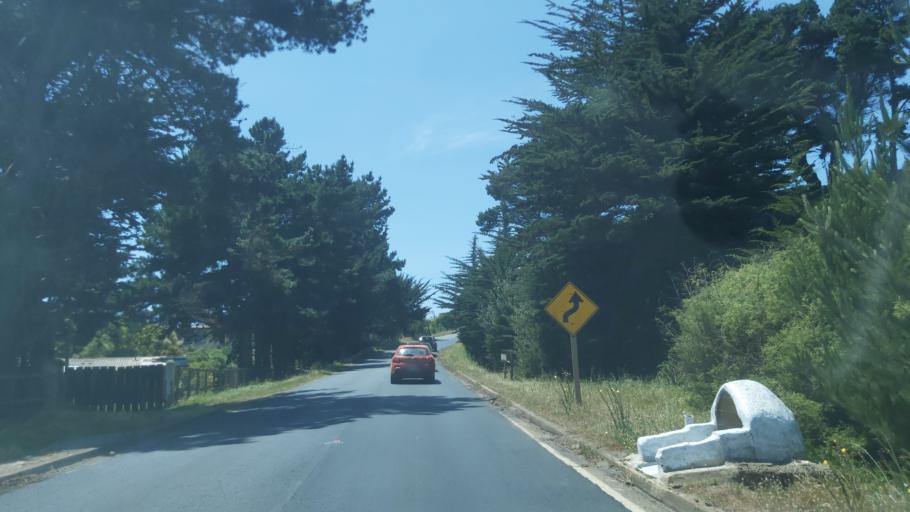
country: CL
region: Maule
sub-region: Provincia de Cauquenes
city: Cauquenes
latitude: -35.8259
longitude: -72.6096
